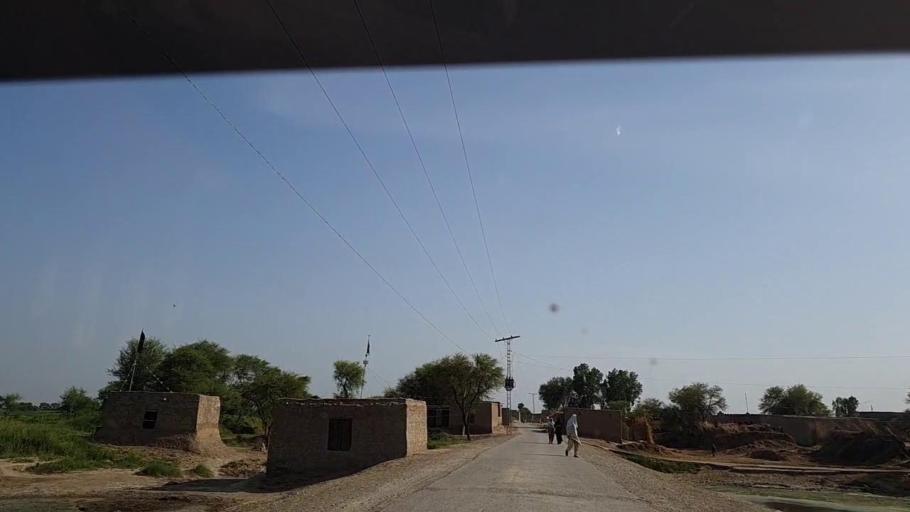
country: PK
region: Sindh
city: Phulji
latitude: 26.9963
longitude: 67.6659
